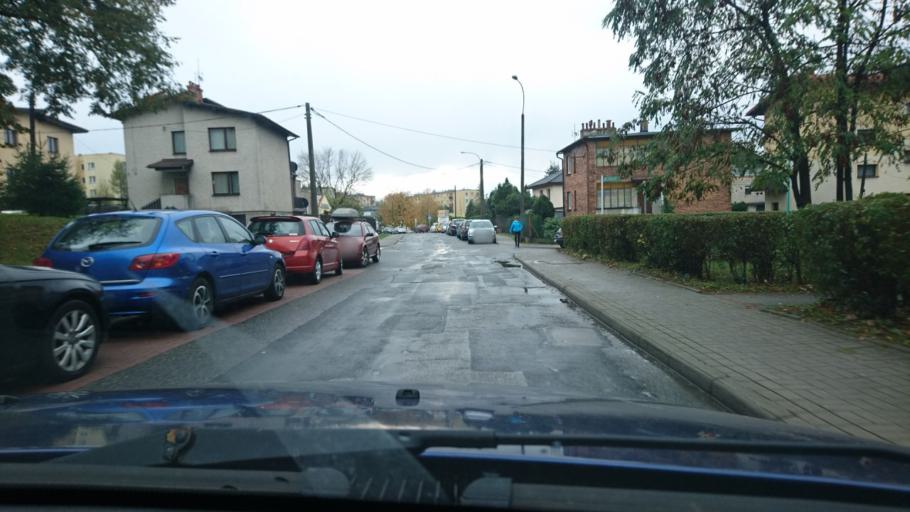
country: PL
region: Silesian Voivodeship
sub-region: Bielsko-Biala
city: Bielsko-Biala
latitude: 49.8049
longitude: 19.0587
